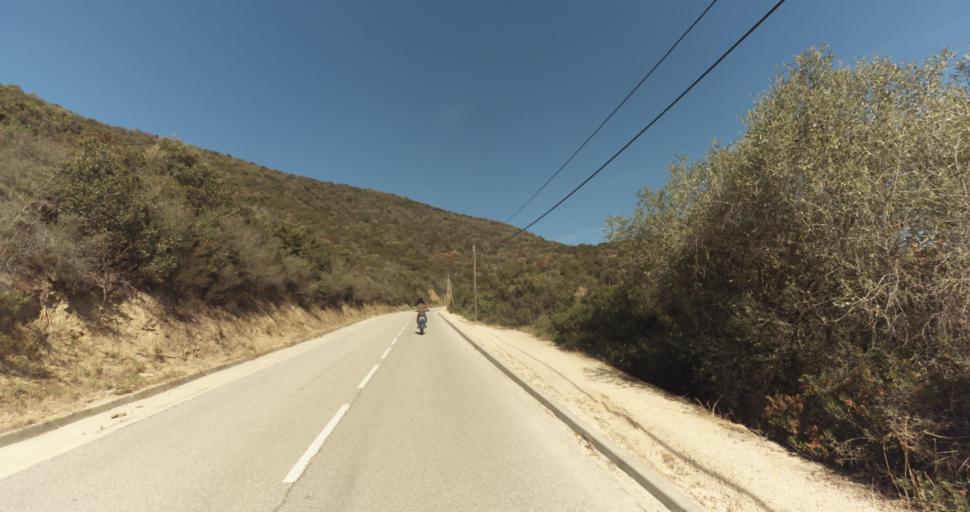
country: FR
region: Corsica
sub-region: Departement de la Corse-du-Sud
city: Ajaccio
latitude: 41.9166
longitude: 8.6424
